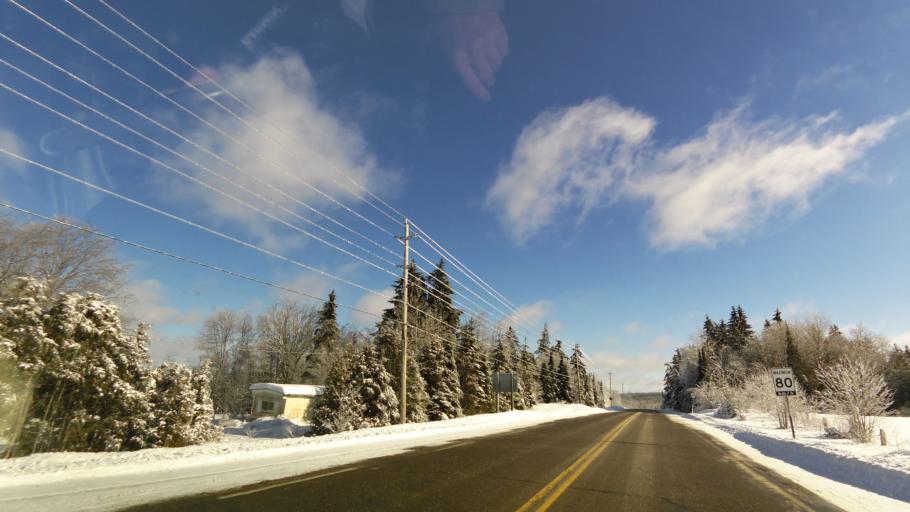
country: CA
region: Ontario
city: Bancroft
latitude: 44.9869
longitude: -78.2922
